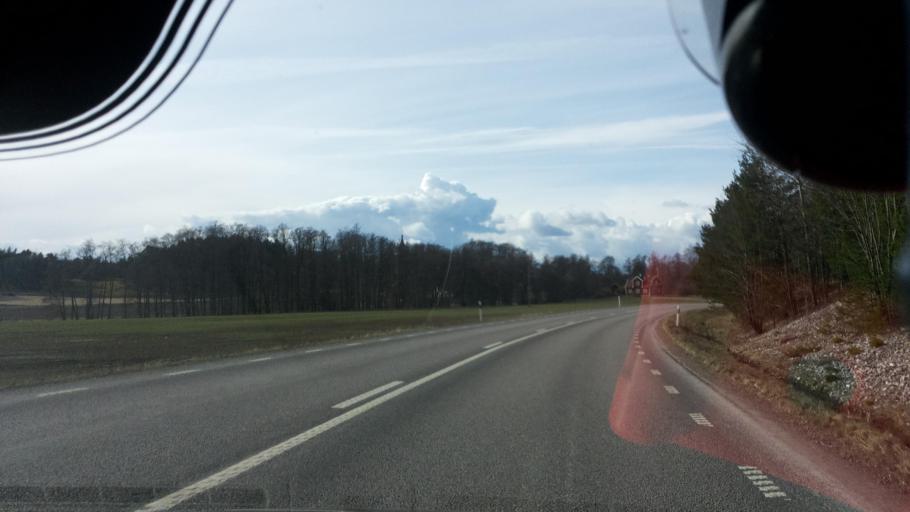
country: SE
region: Soedermanland
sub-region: Trosa Kommun
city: Vagnharad
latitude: 58.9372
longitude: 17.5240
